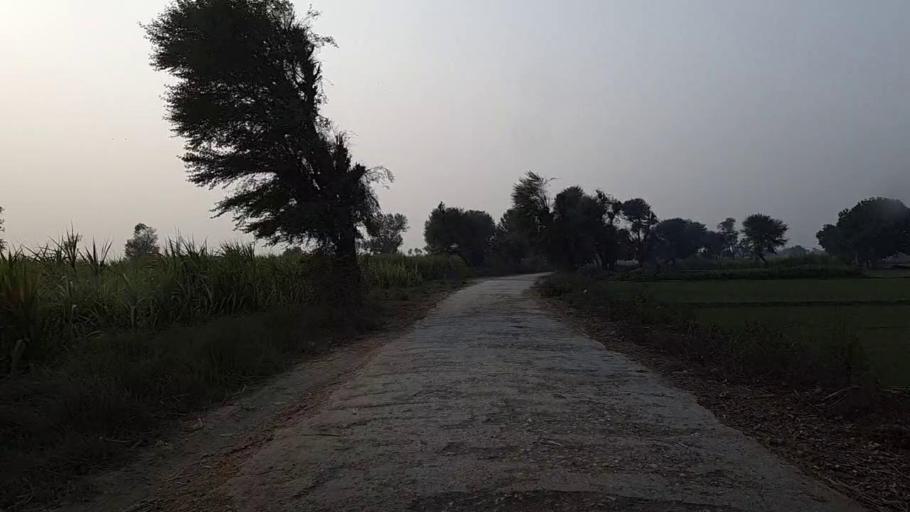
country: PK
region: Sindh
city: Setharja Old
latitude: 27.0810
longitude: 68.5024
